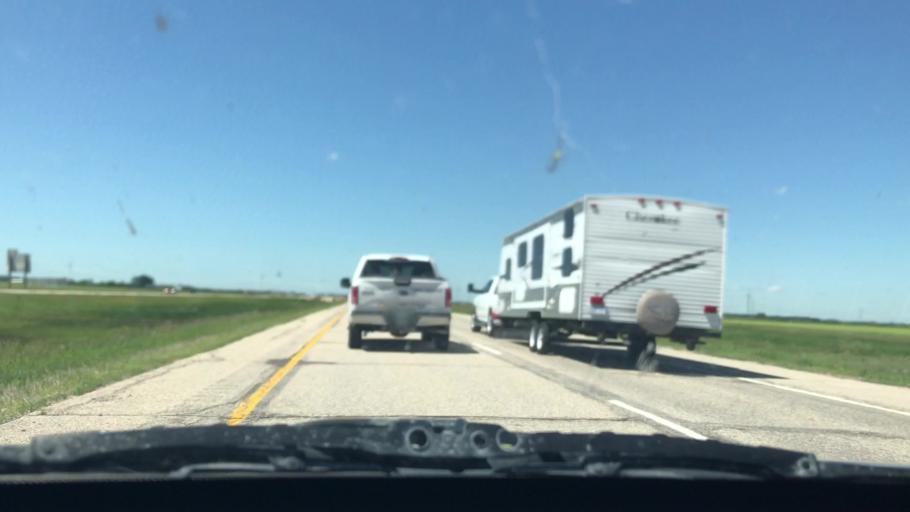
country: CA
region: Manitoba
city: Steinbach
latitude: 49.7052
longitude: -96.6559
